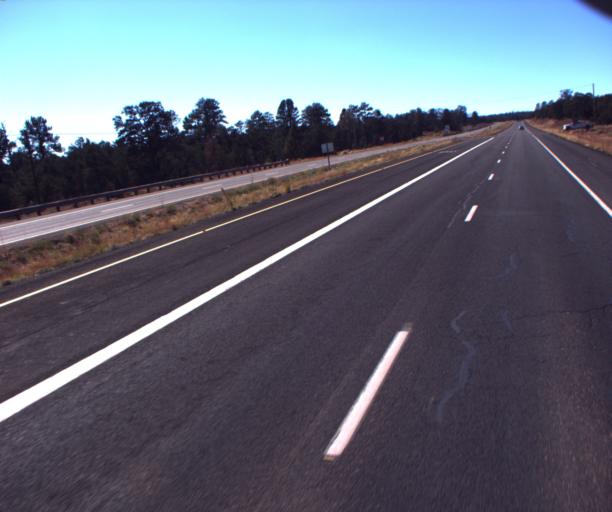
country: US
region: Arizona
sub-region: Apache County
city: Saint Michaels
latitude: 35.6580
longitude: -109.1361
